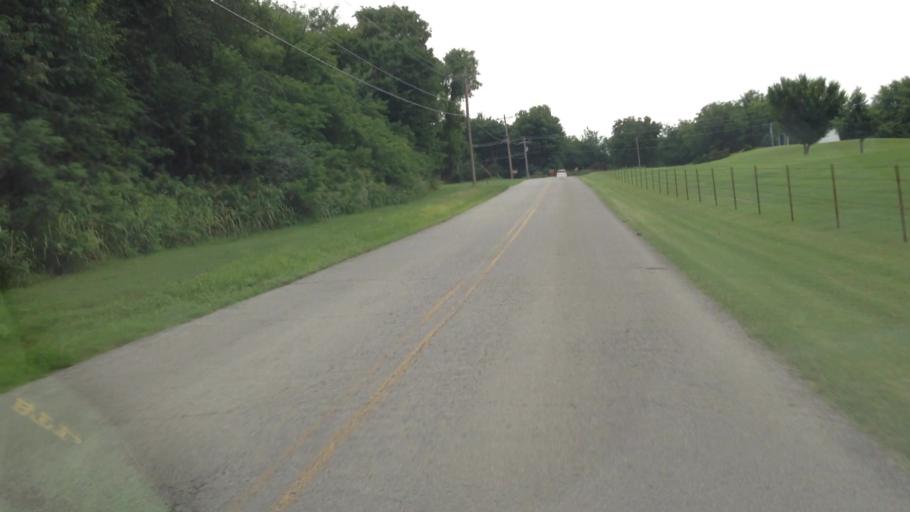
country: US
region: Oklahoma
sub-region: Delaware County
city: Cleora
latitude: 36.5518
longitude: -94.9617
